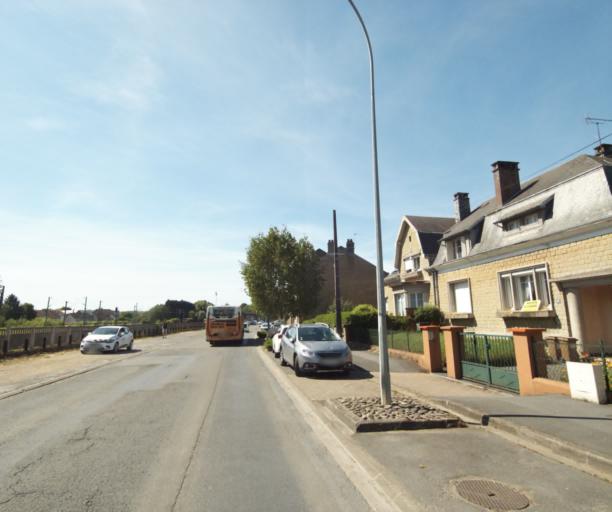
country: FR
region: Champagne-Ardenne
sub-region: Departement des Ardennes
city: Villers-Semeuse
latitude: 49.7482
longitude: 4.7364
